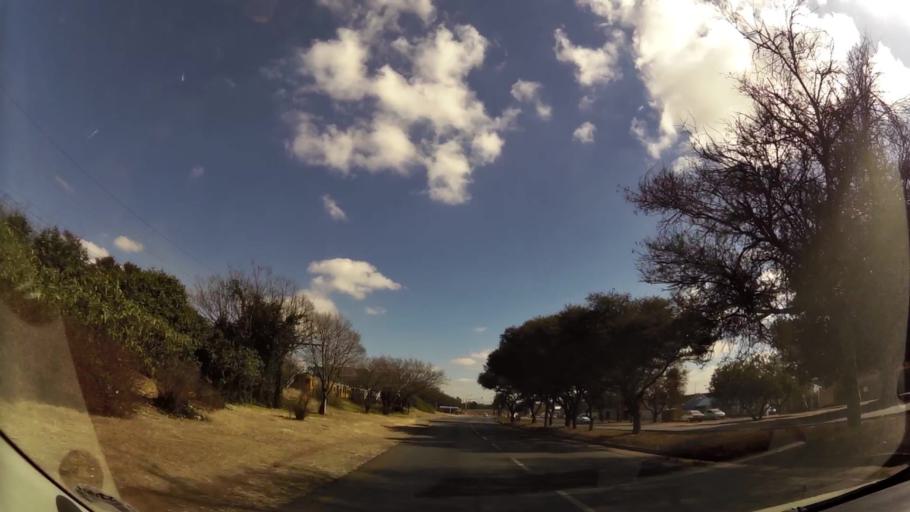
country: ZA
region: Gauteng
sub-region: City of Johannesburg Metropolitan Municipality
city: Roodepoort
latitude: -26.1272
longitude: 27.8319
